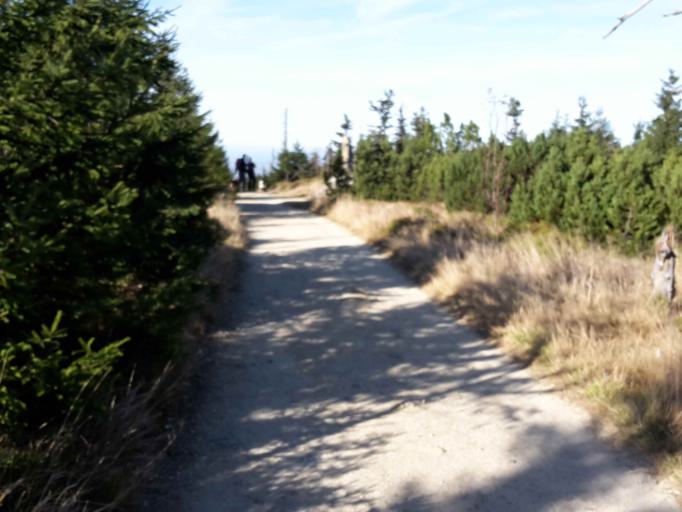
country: CZ
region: Liberecky
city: Nove Mesto pod Smrkem
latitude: 50.8893
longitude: 15.2730
